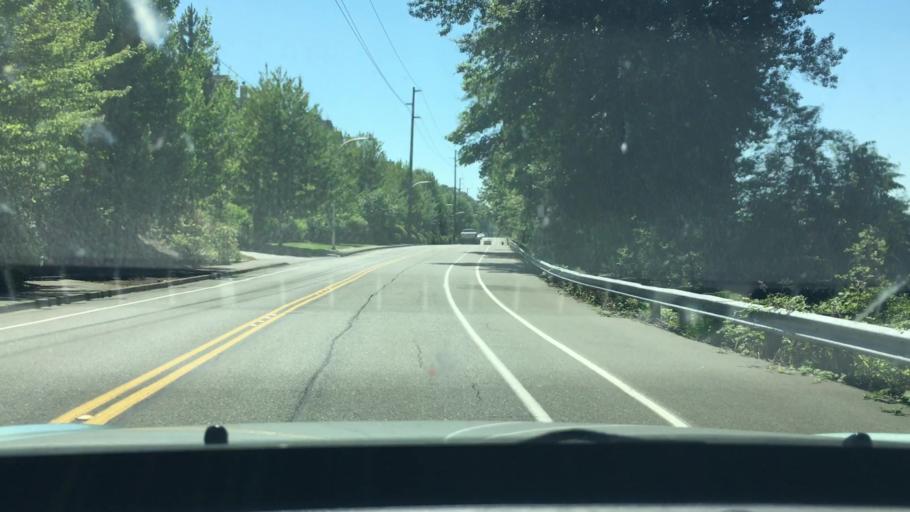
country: US
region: Washington
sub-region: King County
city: Renton
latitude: 47.5133
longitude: -122.2040
